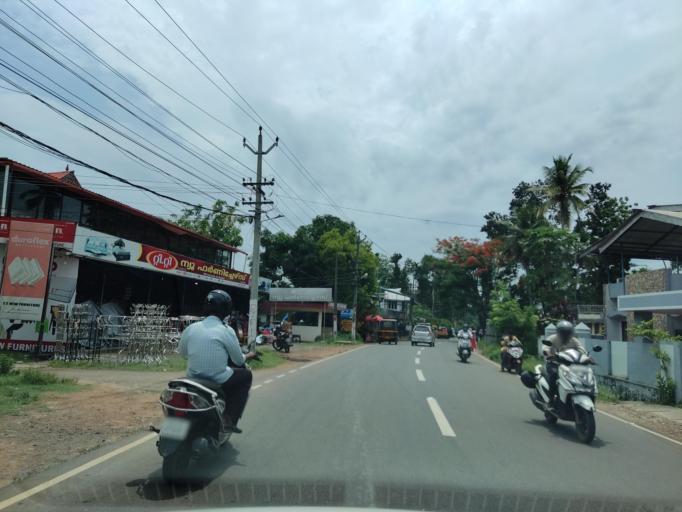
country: IN
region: Kerala
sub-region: Pattanamtitta
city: Adur
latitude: 9.2259
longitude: 76.6677
